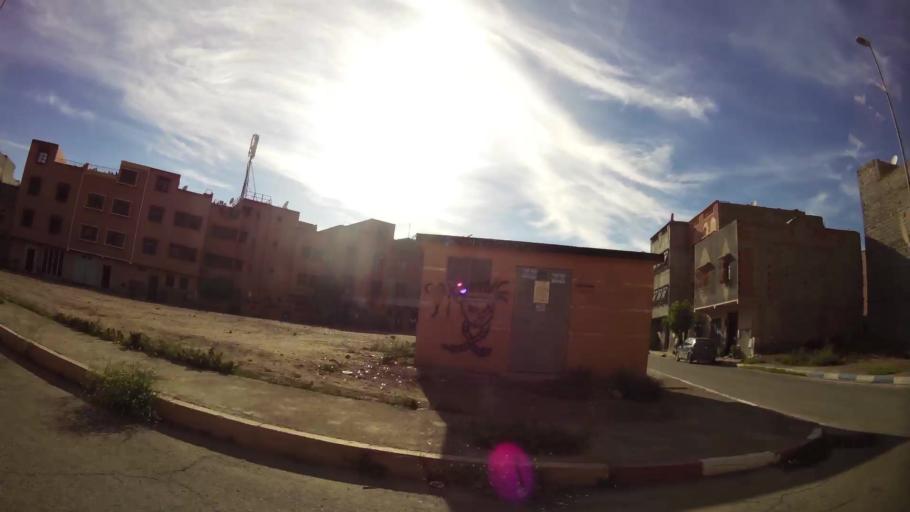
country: MA
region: Marrakech-Tensift-Al Haouz
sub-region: Marrakech
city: Marrakesh
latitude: 31.6883
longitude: -8.0695
